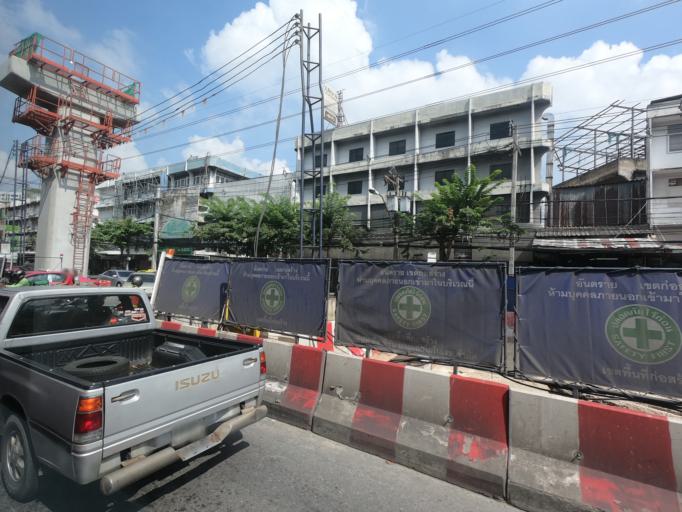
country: TH
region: Bangkok
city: Lat Phrao
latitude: 13.7935
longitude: 100.5961
